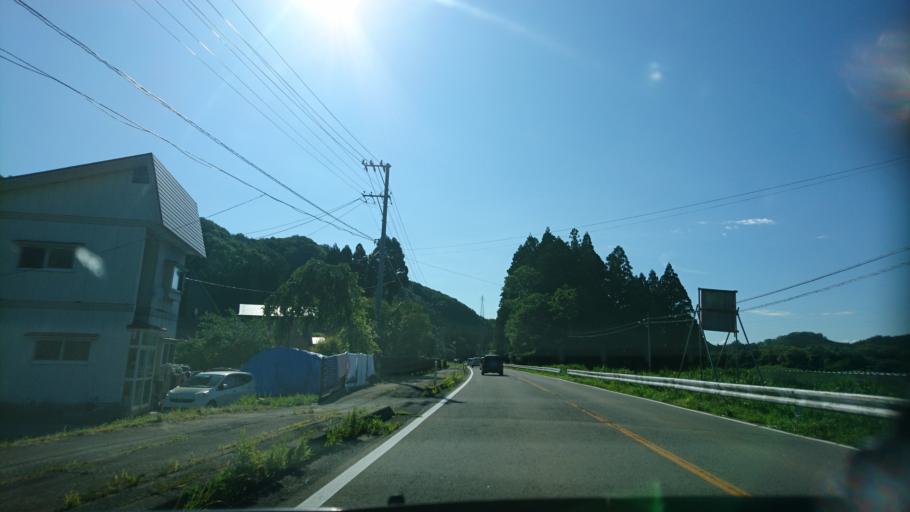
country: JP
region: Akita
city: Kakunodatemachi
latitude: 39.6189
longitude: 140.4775
